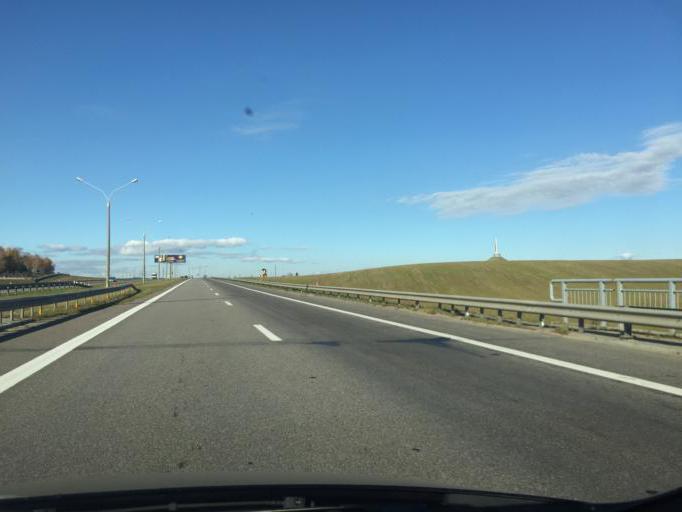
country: BY
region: Minsk
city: Slabada
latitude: 54.0087
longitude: 27.9023
